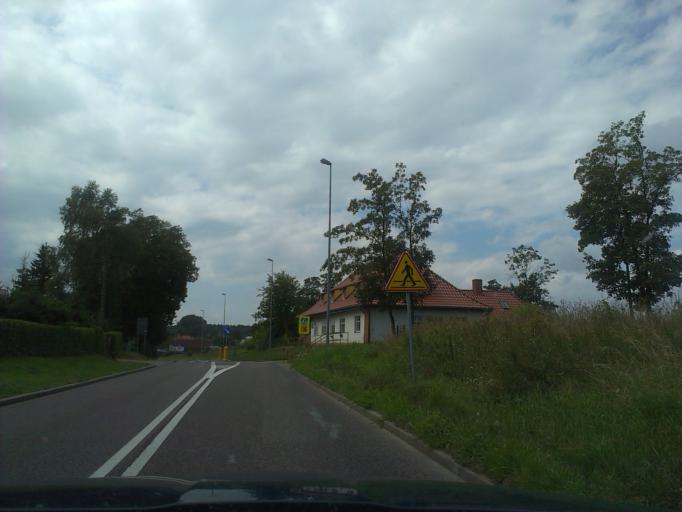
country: PL
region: West Pomeranian Voivodeship
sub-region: Powiat kamienski
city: Wolin
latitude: 53.9691
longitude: 14.6182
